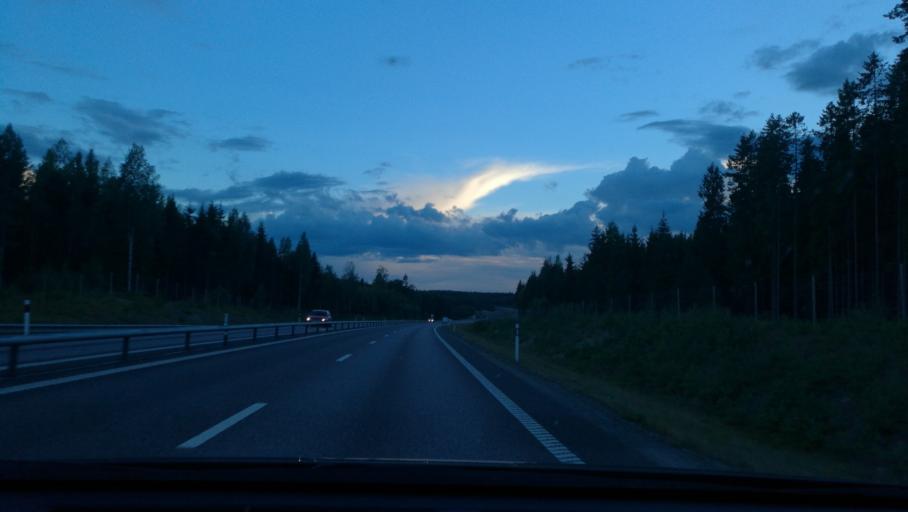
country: SE
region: Soedermanland
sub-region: Katrineholms Kommun
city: Katrineholm
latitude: 58.9646
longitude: 16.2487
